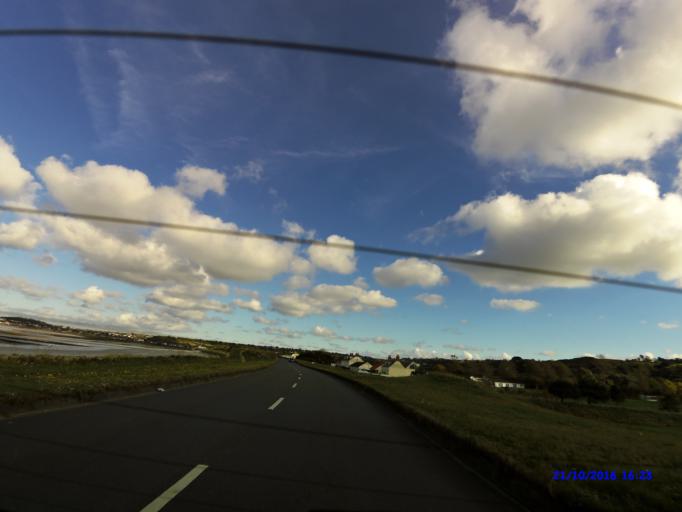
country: GG
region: St Peter Port
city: Saint Peter Port
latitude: 49.4631
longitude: -2.6221
